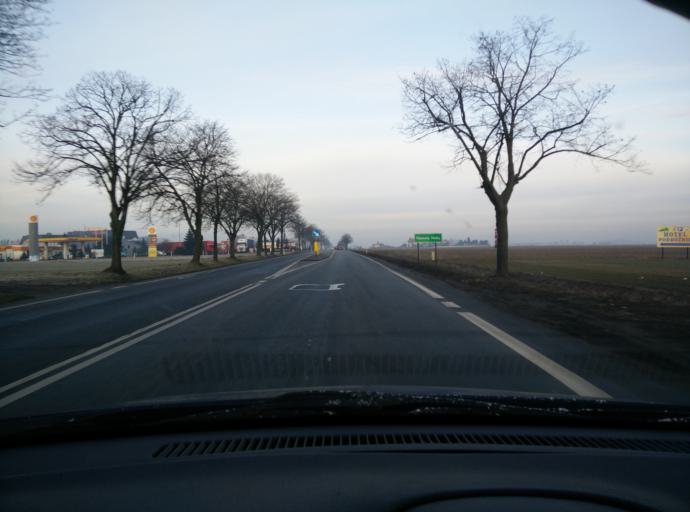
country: PL
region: Greater Poland Voivodeship
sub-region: Powiat sredzki
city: Zaniemysl
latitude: 52.2336
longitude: 17.1797
